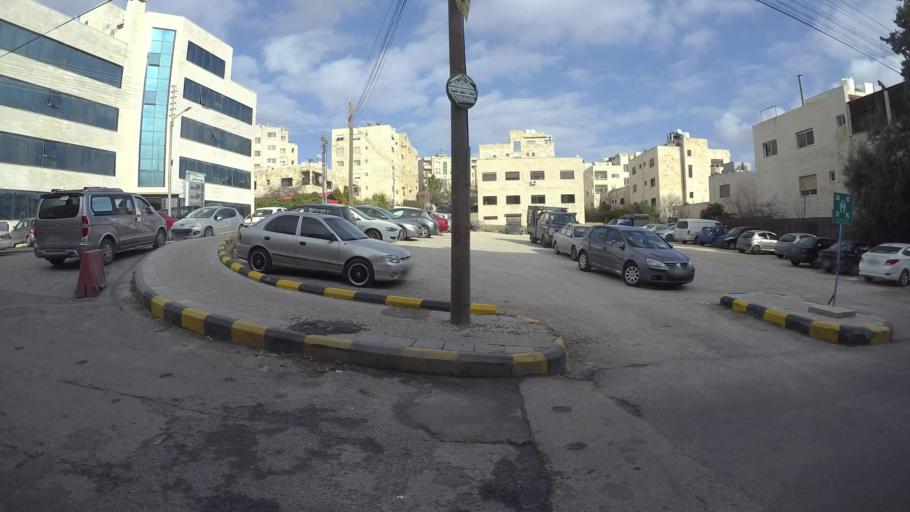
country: JO
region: Amman
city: Wadi as Sir
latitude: 31.9774
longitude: 35.8446
